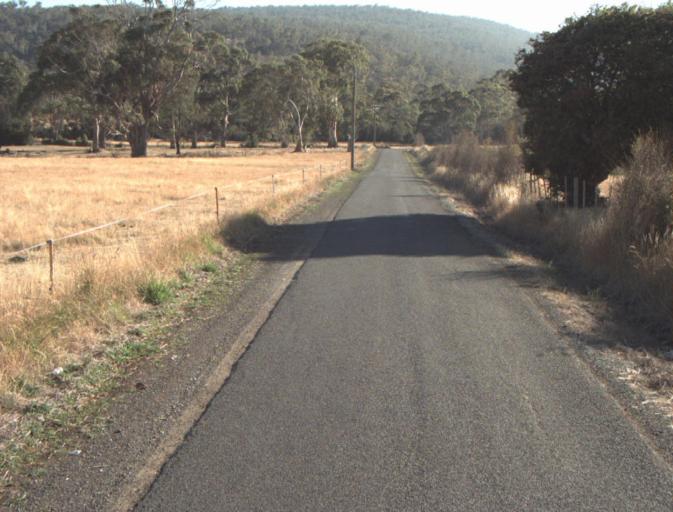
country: AU
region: Tasmania
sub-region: Launceston
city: Newstead
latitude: -41.4355
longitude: 147.2124
